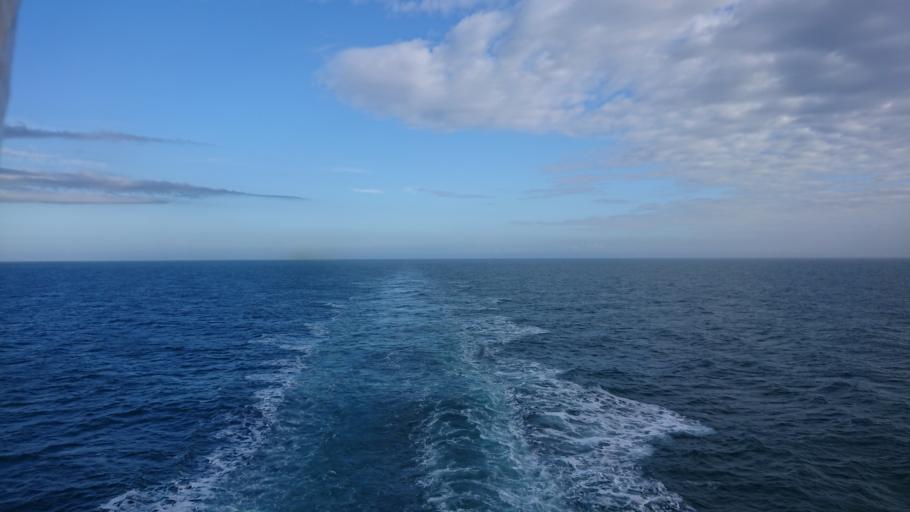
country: GB
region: Wales
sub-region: Pembrokeshire
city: Saint David's
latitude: 52.1352
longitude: -5.6197
